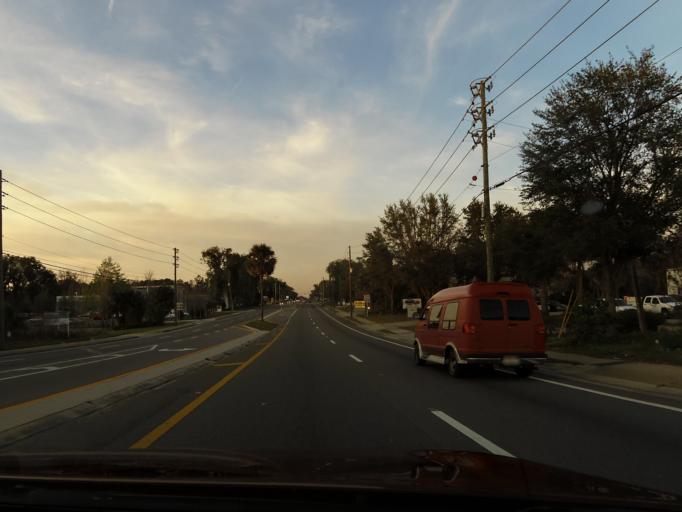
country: US
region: Florida
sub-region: Volusia County
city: North DeLand
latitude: 29.0576
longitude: -81.3044
